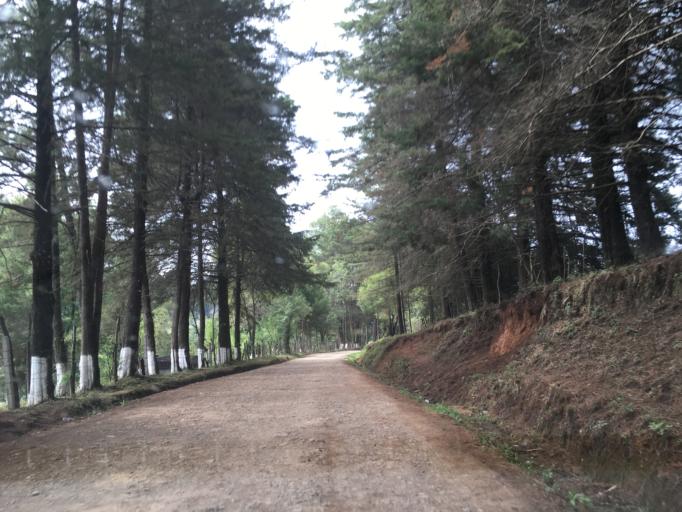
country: MX
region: Michoacan
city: Acuitzio del Canje
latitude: 19.5093
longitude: -101.2154
